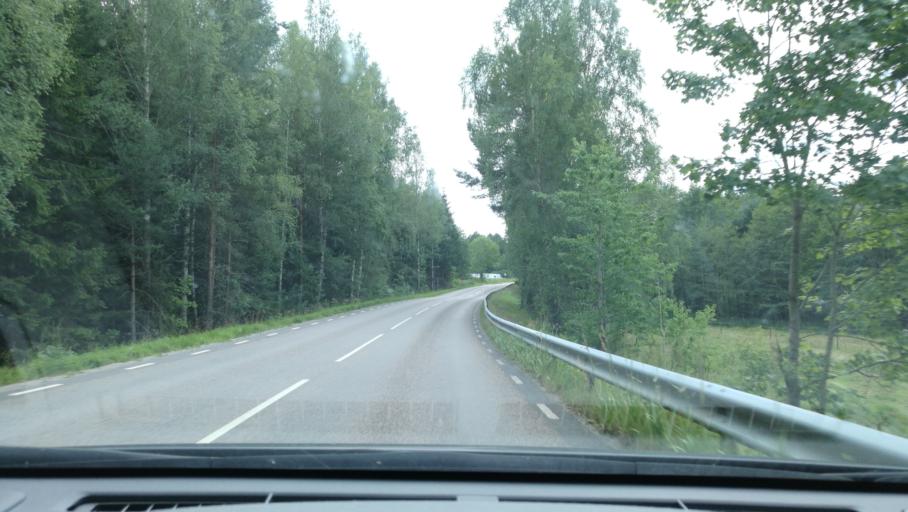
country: SE
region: OEstergoetland
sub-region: Norrkopings Kommun
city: Krokek
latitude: 58.6667
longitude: 16.4095
